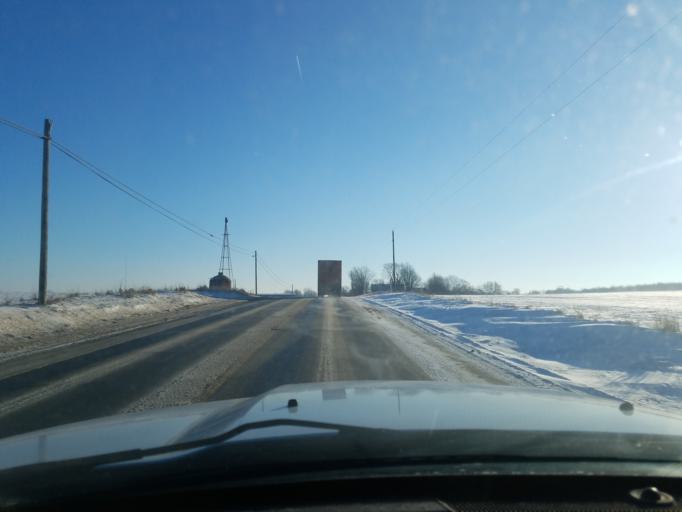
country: US
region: Indiana
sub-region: Noble County
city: Kendallville
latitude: 41.4524
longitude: -85.3174
